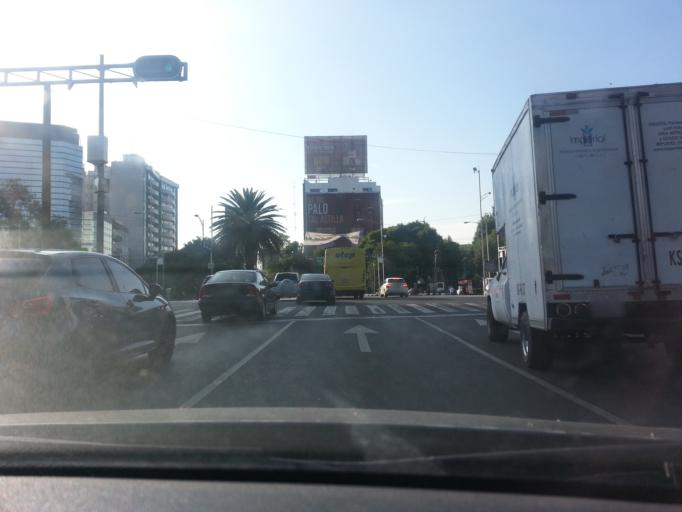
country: MX
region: Mexico City
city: Alvaro Obregon
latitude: 19.3680
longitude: -99.1813
